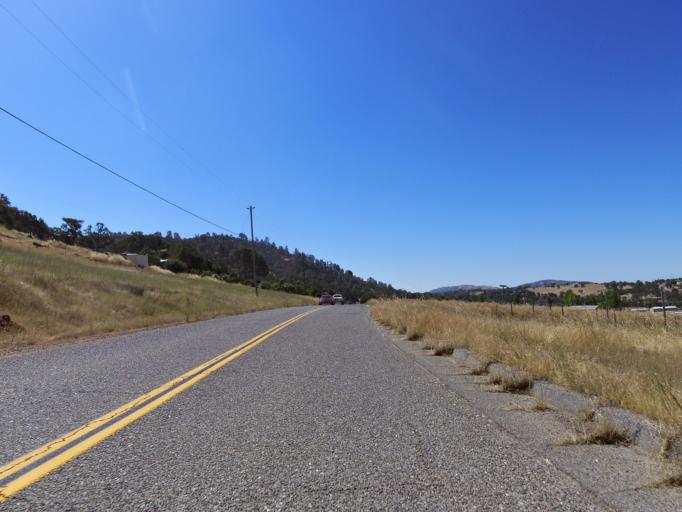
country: US
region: California
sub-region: Tuolumne County
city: Jamestown
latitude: 37.6868
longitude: -120.3256
